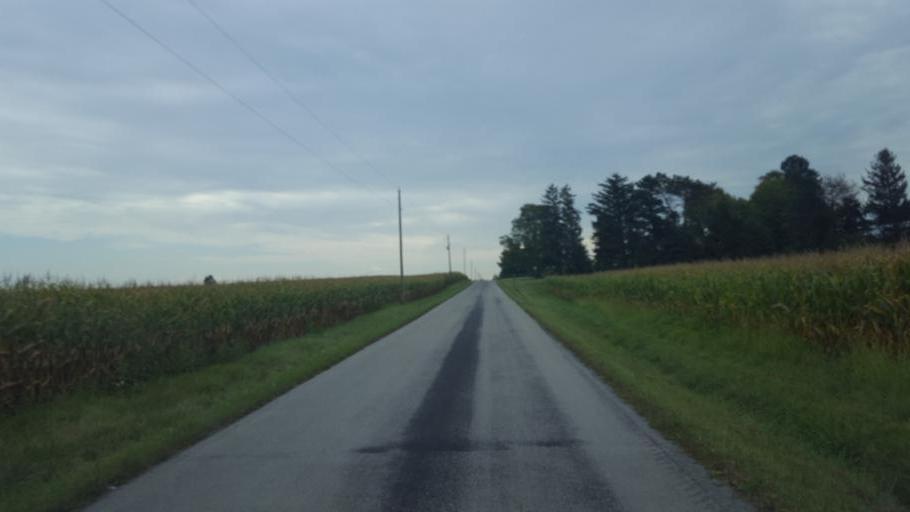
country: US
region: Ohio
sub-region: Wyandot County
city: Upper Sandusky
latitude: 40.9062
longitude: -83.1775
